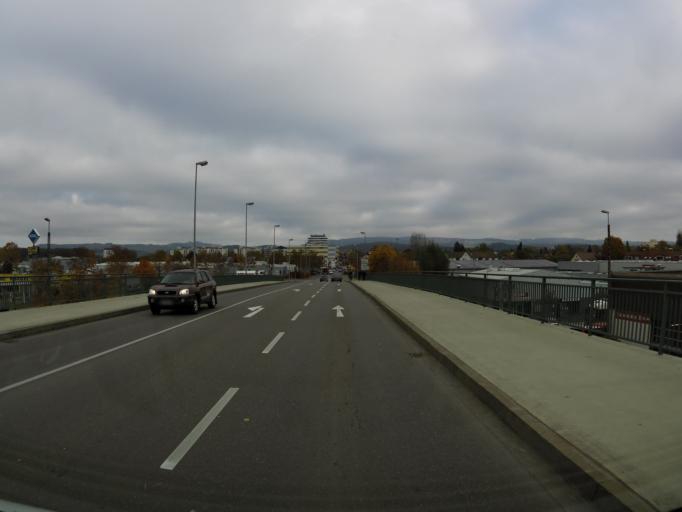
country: DE
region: Baden-Wuerttemberg
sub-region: Freiburg Region
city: Radolfzell am Bodensee
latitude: 47.7407
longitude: 8.9556
